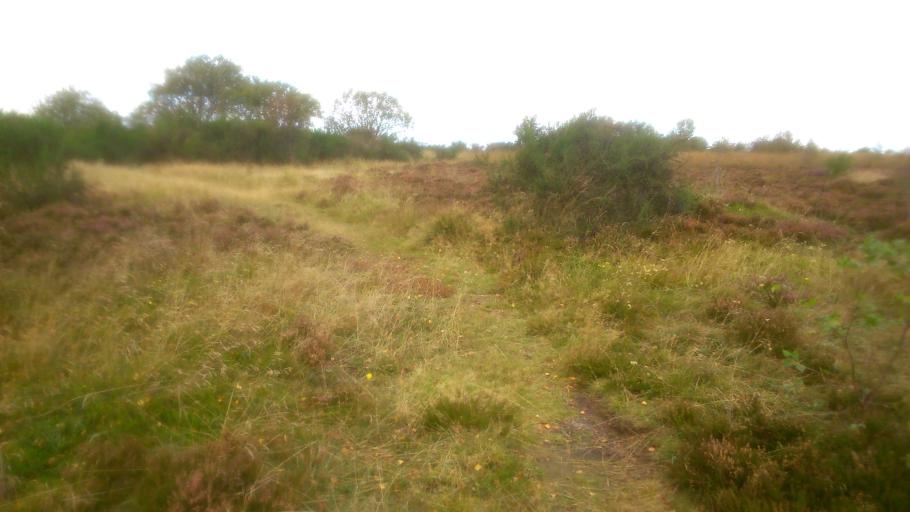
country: DK
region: Central Jutland
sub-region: Ringkobing-Skjern Kommune
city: Skjern
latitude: 56.0488
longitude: 8.4430
